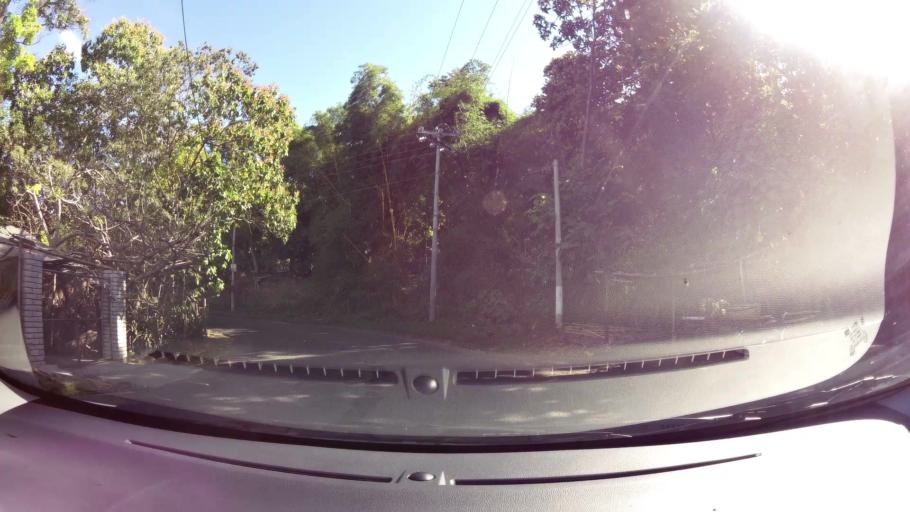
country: SV
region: Cuscatlan
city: Suchitoto
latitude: 13.9285
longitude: -89.0359
